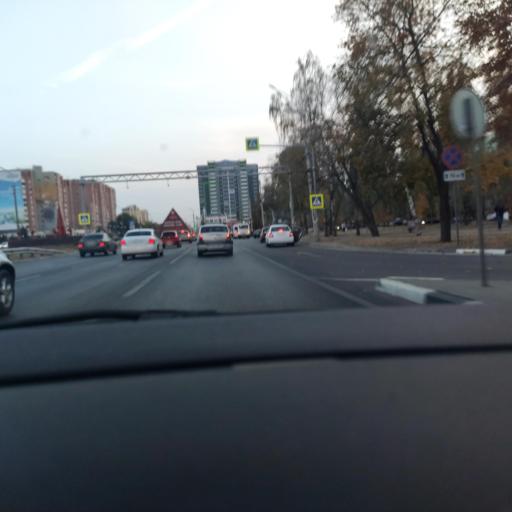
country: RU
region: Voronezj
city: Voronezh
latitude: 51.7050
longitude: 39.1811
